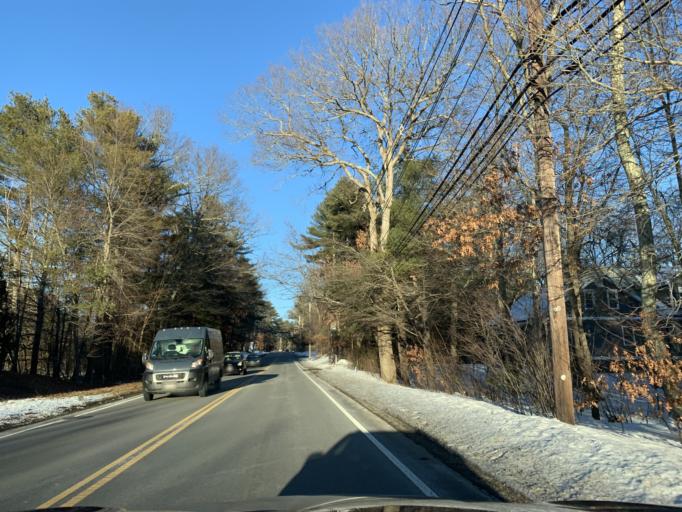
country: US
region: Massachusetts
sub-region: Bristol County
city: Easton
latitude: 41.9957
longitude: -71.1517
